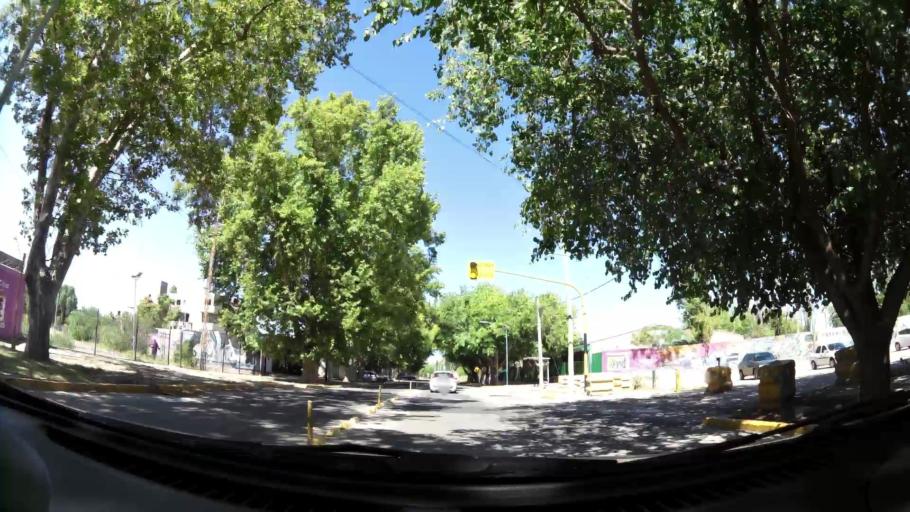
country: AR
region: Mendoza
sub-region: Departamento de Godoy Cruz
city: Godoy Cruz
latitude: -32.9533
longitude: -68.8514
